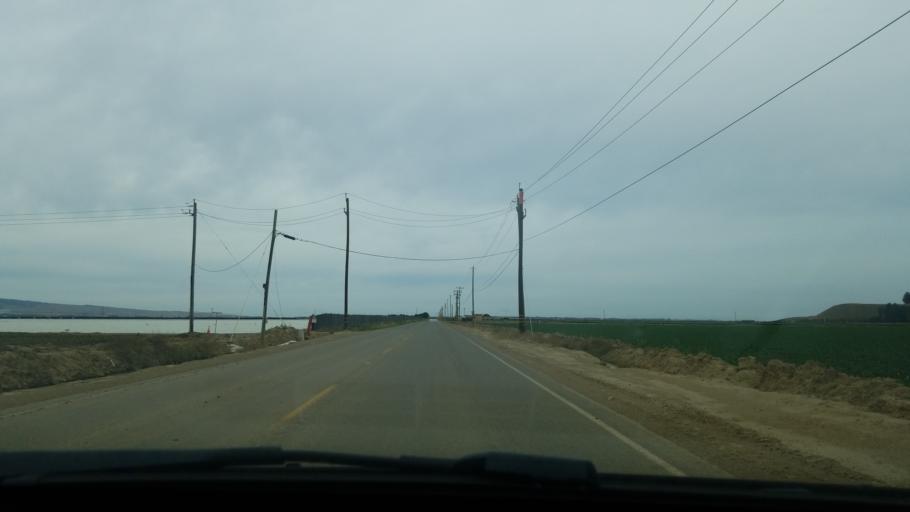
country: US
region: California
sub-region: San Luis Obispo County
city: Nipomo
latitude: 35.0051
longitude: -120.5106
